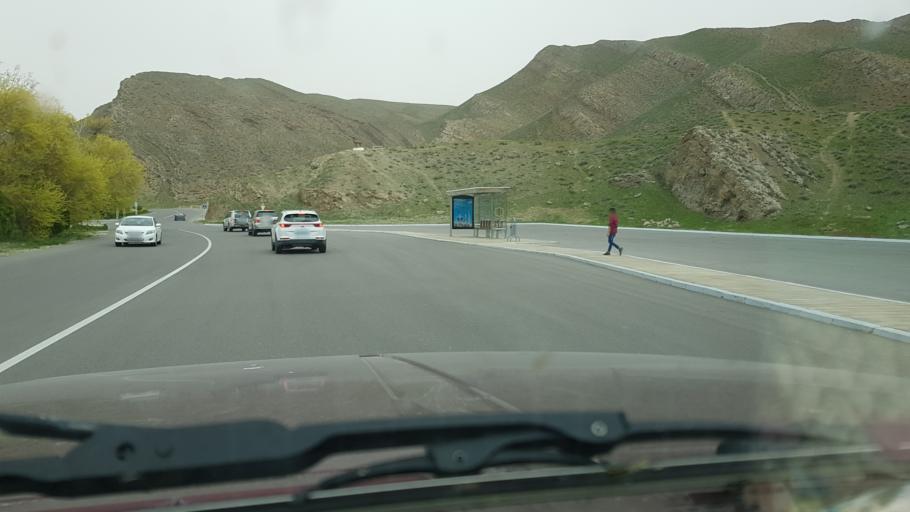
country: TM
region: Ahal
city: Arcabil
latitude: 38.0228
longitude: 58.0054
